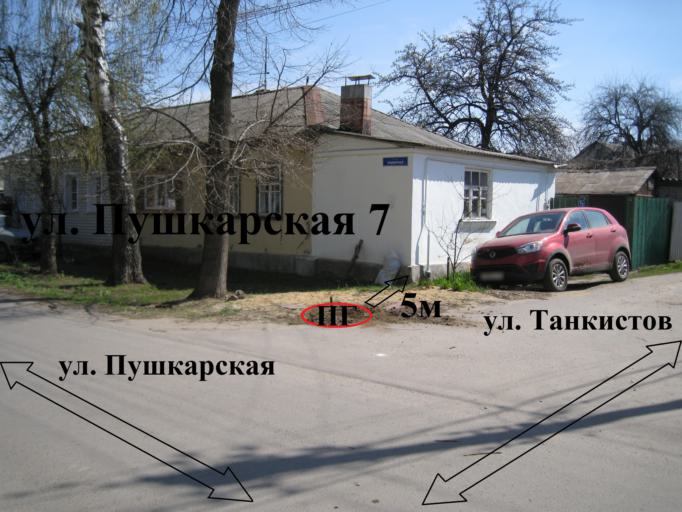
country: RU
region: Voronezj
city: Voronezh
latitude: 51.6459
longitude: 39.1781
